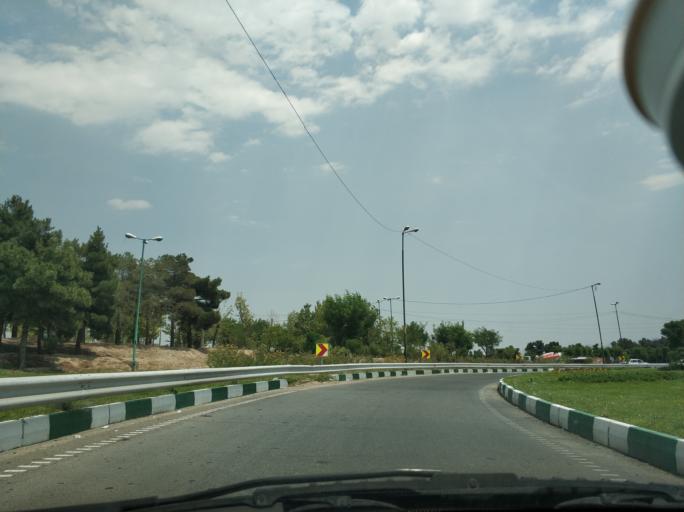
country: IR
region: Tehran
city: Tajrish
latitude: 35.7715
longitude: 51.5571
